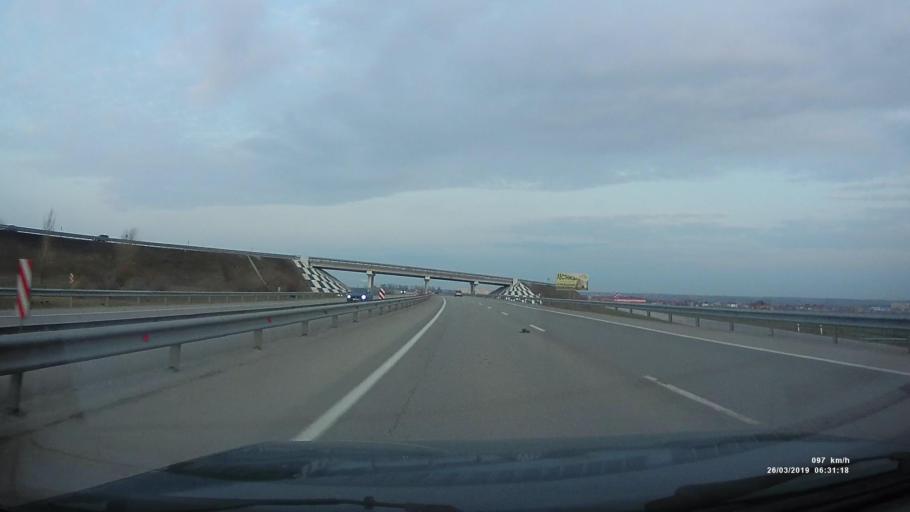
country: RU
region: Rostov
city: Krym
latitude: 47.2735
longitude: 39.5341
